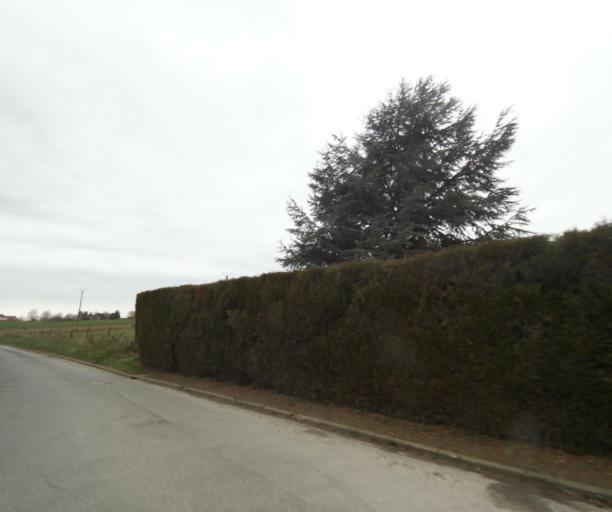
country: FR
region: Nord-Pas-de-Calais
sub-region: Departement du Nord
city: Sebourg
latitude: 50.3523
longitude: 3.6447
